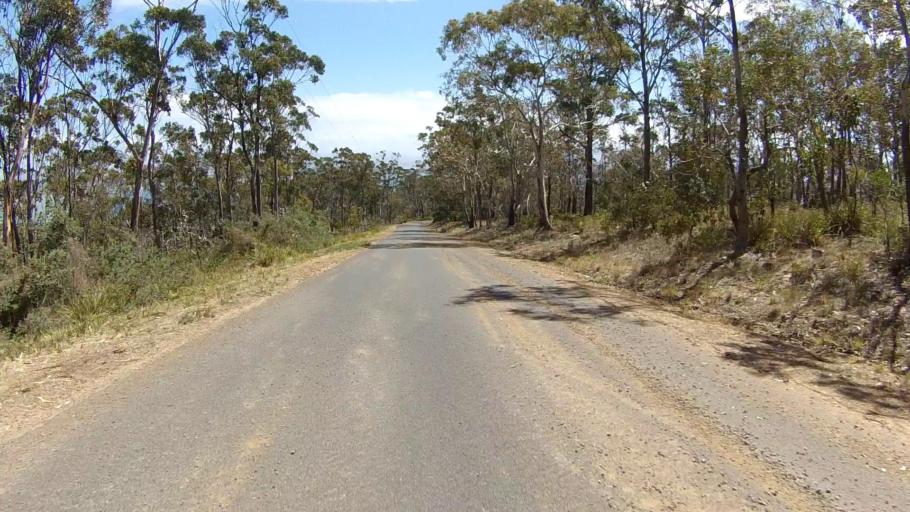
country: AU
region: Tasmania
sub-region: Clarence
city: Sandford
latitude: -43.0130
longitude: 147.4771
